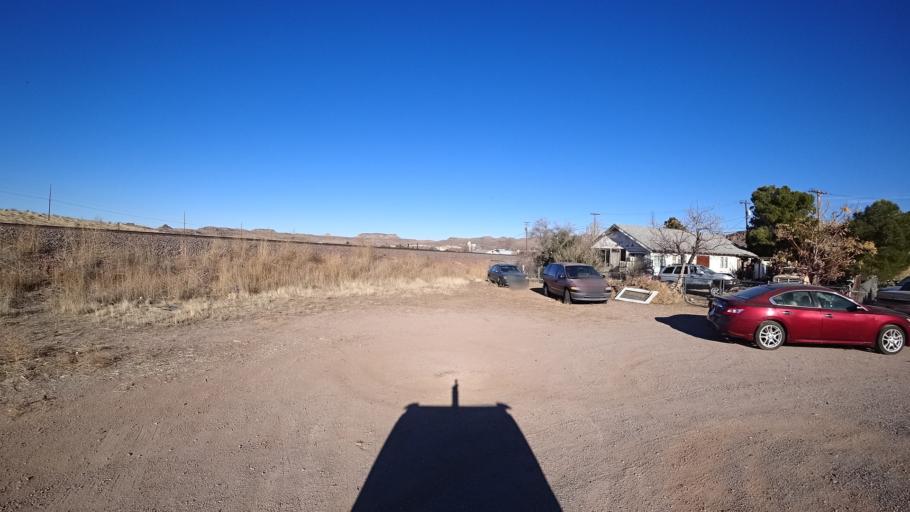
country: US
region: Arizona
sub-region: Mohave County
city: Kingman
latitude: 35.1855
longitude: -114.0459
